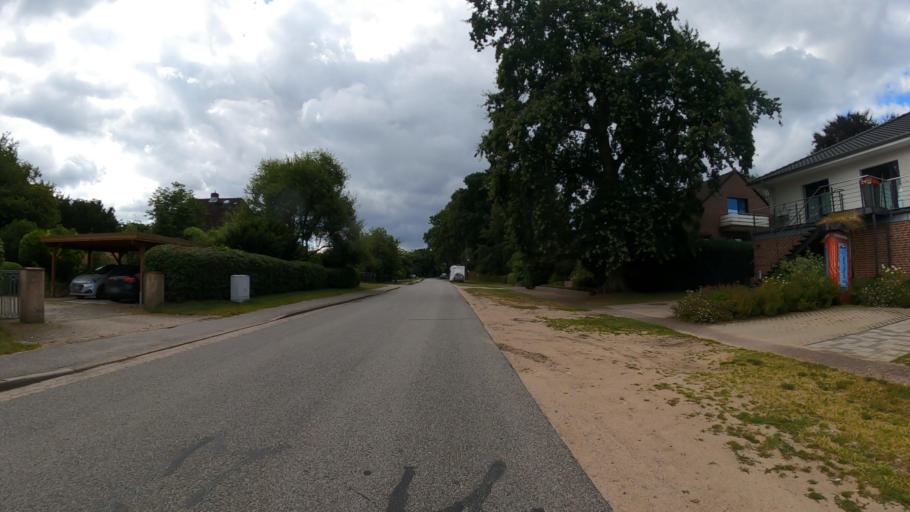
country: DE
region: Schleswig-Holstein
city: Padenstedt
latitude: 54.0473
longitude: 9.9154
